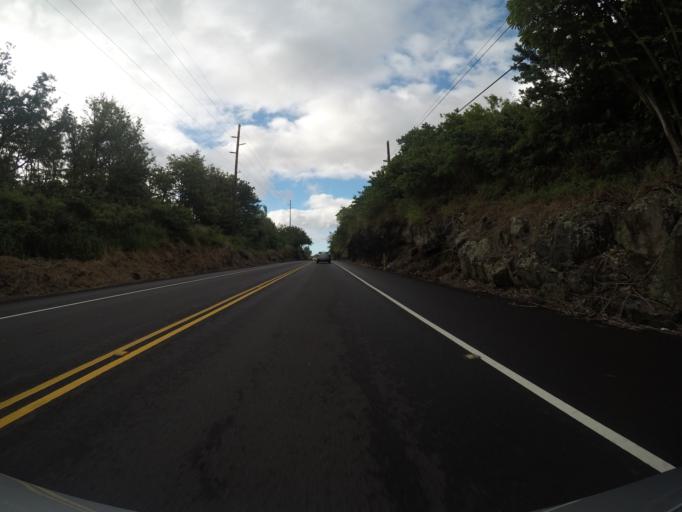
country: US
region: Hawaii
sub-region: Hawaii County
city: Kalaoa
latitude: 19.7475
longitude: -155.9741
